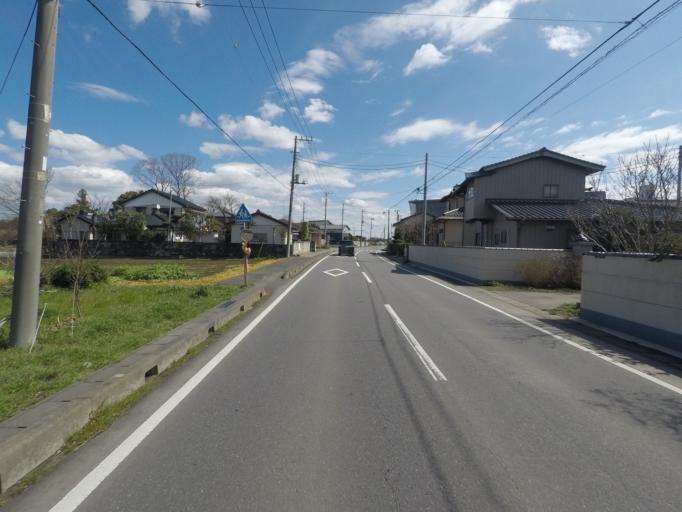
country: JP
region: Ibaraki
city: Fujishiro
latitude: 35.9471
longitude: 140.0832
